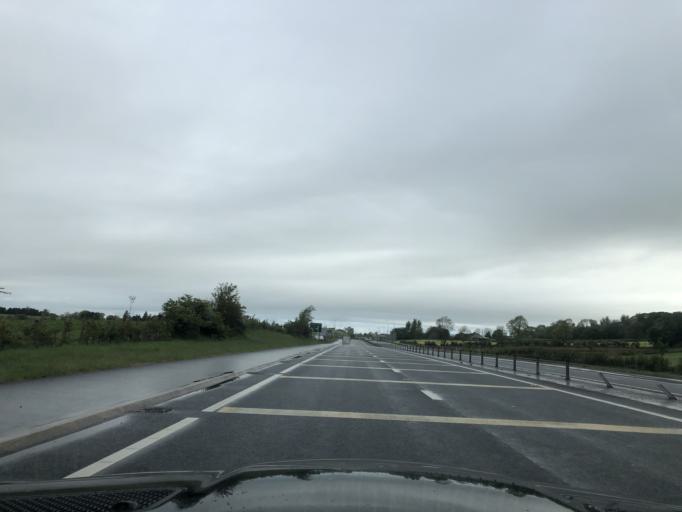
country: GB
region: Northern Ireland
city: Dunloy
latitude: 55.0126
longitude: -6.3648
